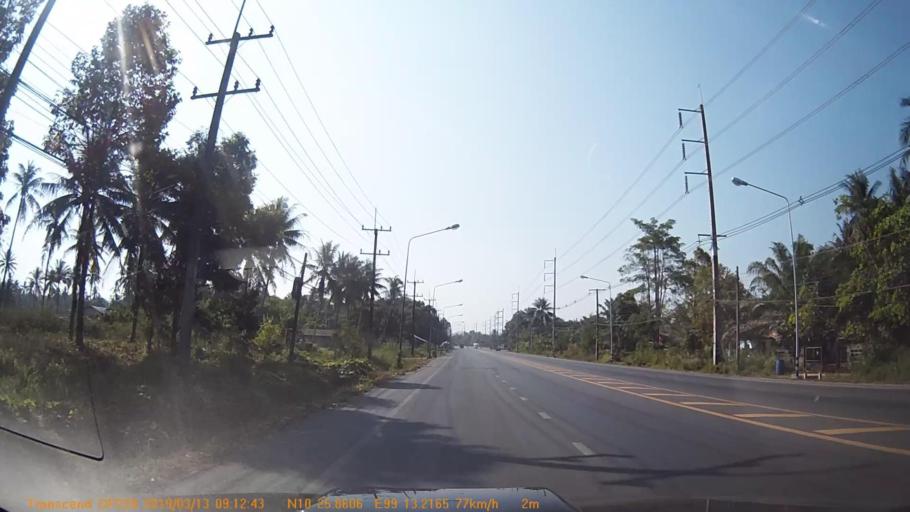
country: TH
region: Chumphon
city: Chumphon
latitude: 10.4307
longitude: 99.2204
